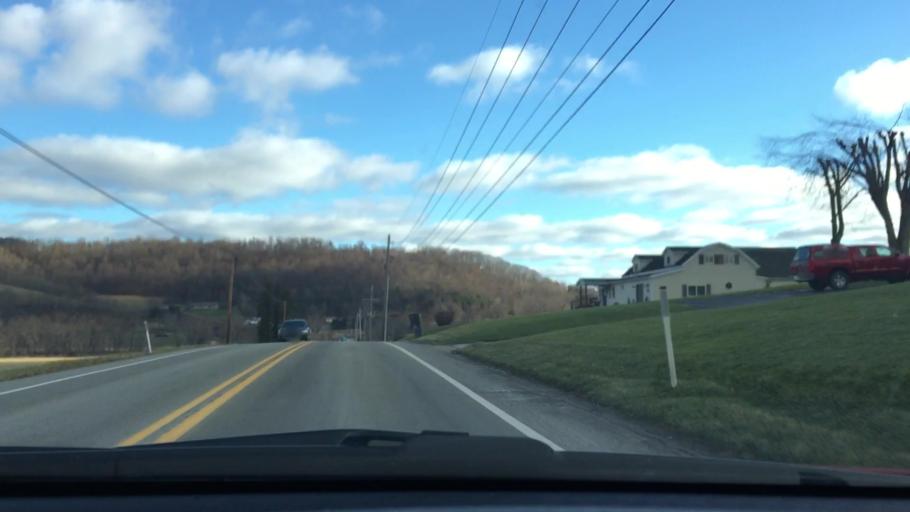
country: US
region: Pennsylvania
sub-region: Indiana County
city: Indiana
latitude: 40.6548
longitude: -79.3108
